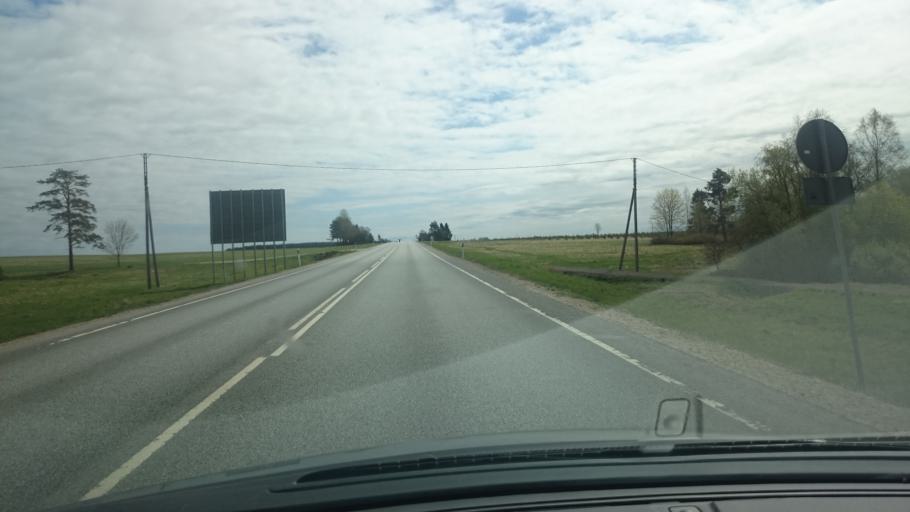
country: EE
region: Laeaene-Virumaa
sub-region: Haljala vald
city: Haljala
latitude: 59.4210
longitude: 26.2959
